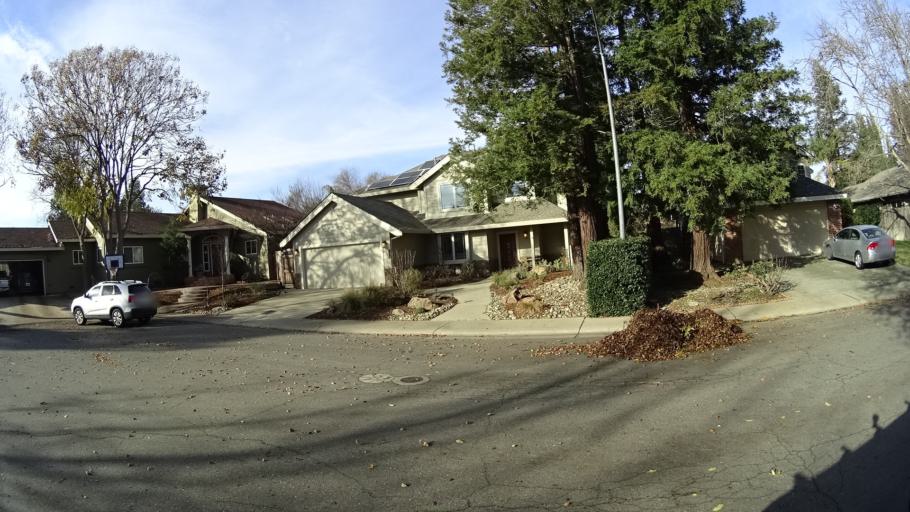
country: US
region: California
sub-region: Yolo County
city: Davis
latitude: 38.5443
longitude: -121.7074
